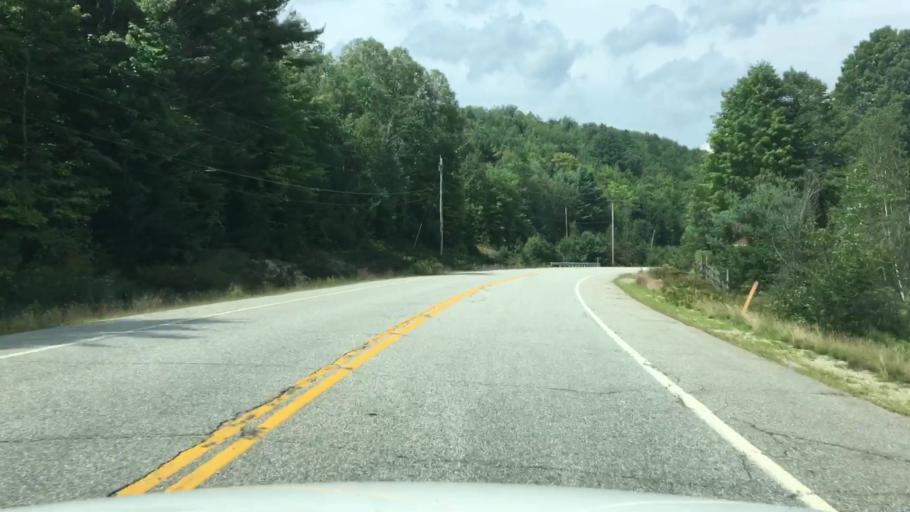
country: US
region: Maine
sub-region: Oxford County
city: Rumford
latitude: 44.5497
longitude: -70.7085
